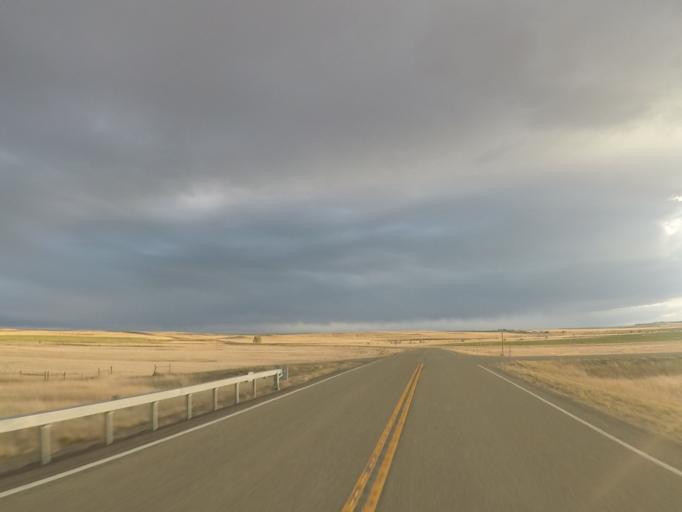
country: US
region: Montana
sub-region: Golden Valley County
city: Ryegate
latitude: 46.3699
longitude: -109.2655
